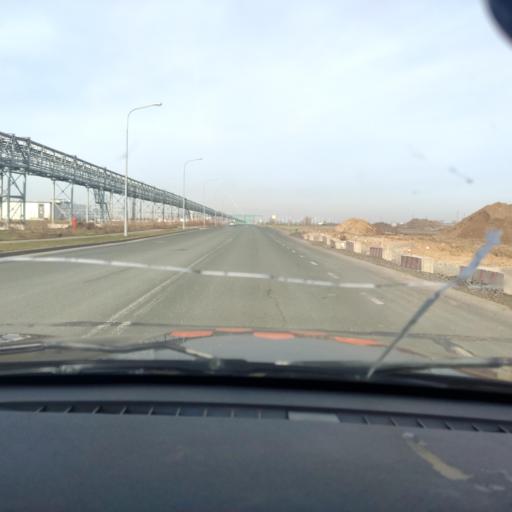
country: RU
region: Samara
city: Podstepki
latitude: 53.5608
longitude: 49.1891
